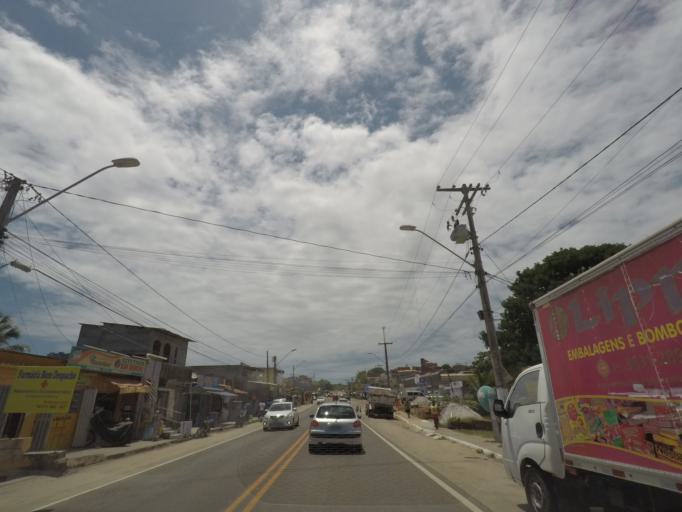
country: BR
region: Bahia
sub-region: Itaparica
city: Itaparica
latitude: -12.9314
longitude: -38.6225
